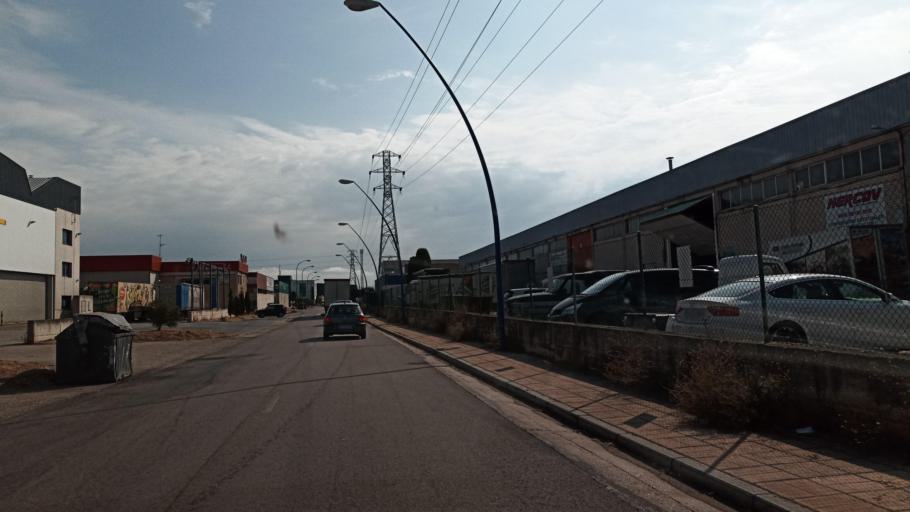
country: ES
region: Castille and Leon
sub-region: Provincia de Burgos
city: Burgos
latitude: 42.3629
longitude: -3.6464
